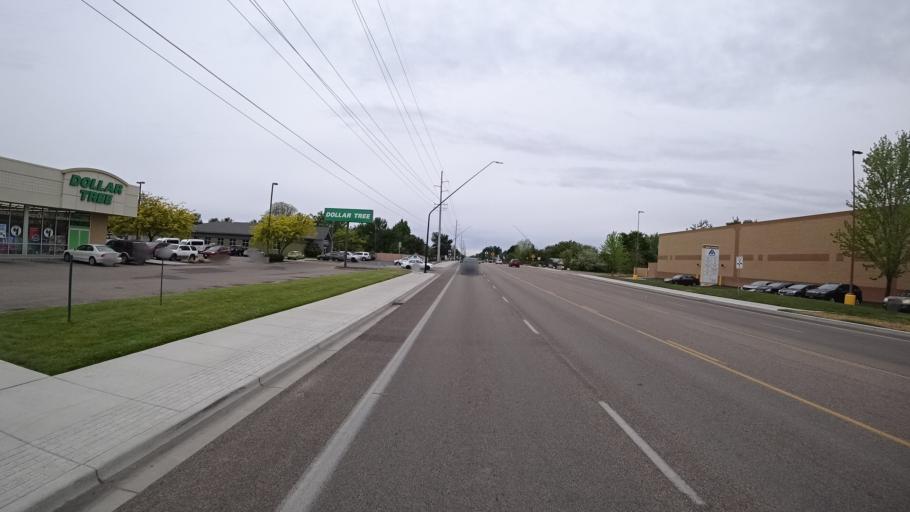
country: US
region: Idaho
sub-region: Ada County
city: Eagle
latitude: 43.6339
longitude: -116.3160
